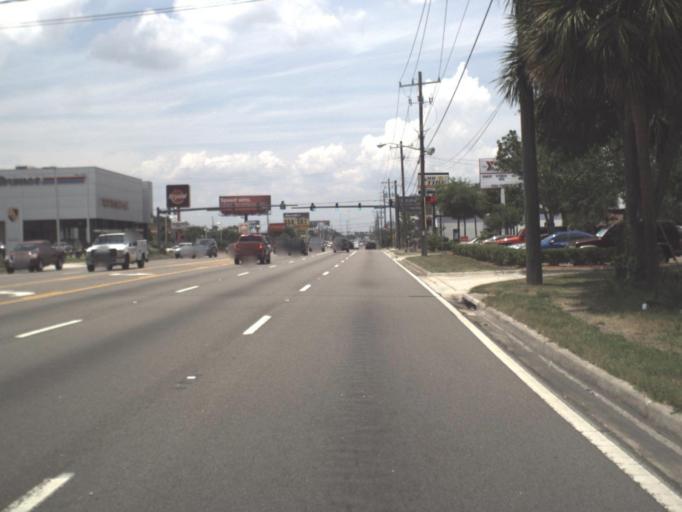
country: US
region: Florida
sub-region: Duval County
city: Jacksonville
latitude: 30.3232
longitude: -81.5367
